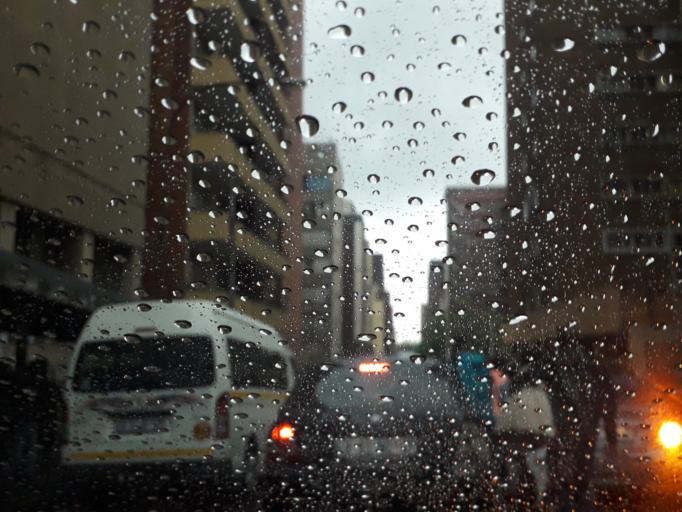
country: ZA
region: Gauteng
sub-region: City of Johannesburg Metropolitan Municipality
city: Johannesburg
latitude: -26.1870
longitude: 28.0498
